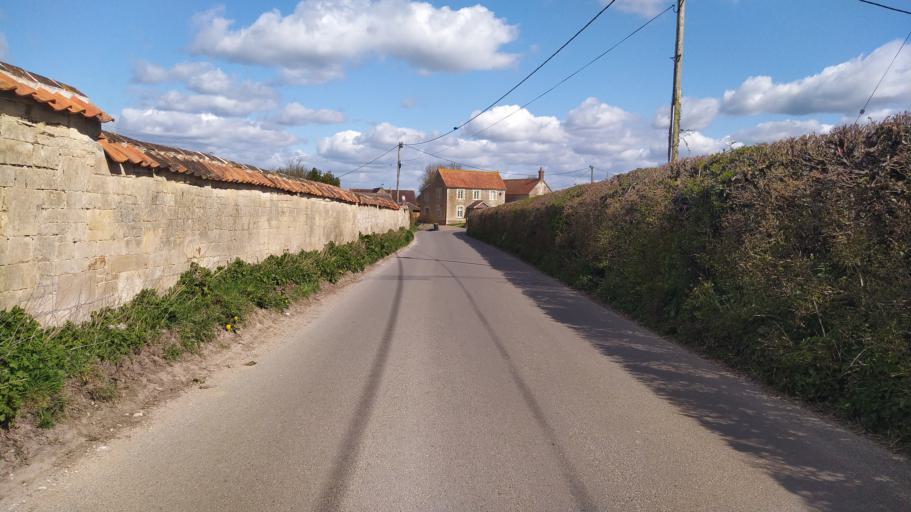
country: GB
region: England
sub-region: Dorset
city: Sturminster Newton
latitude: 50.9634
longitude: -2.3261
